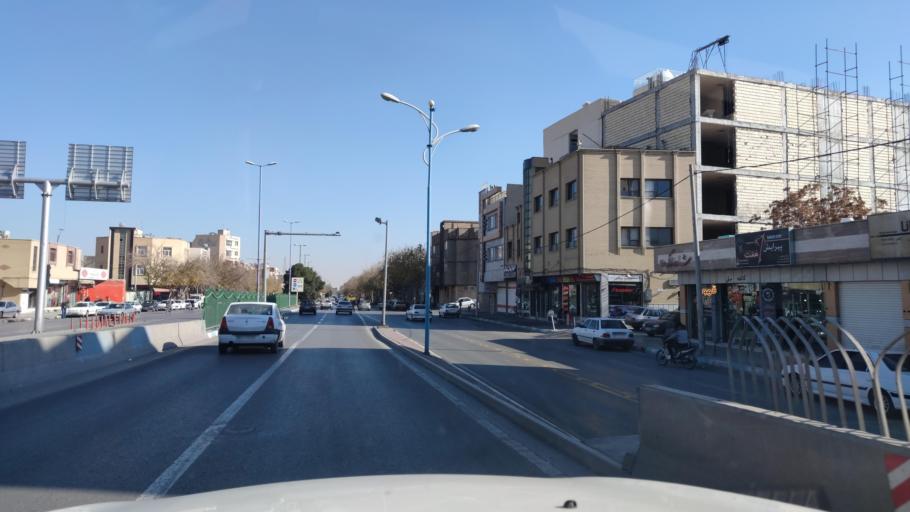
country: IR
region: Isfahan
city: Isfahan
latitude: 32.6789
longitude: 51.6748
